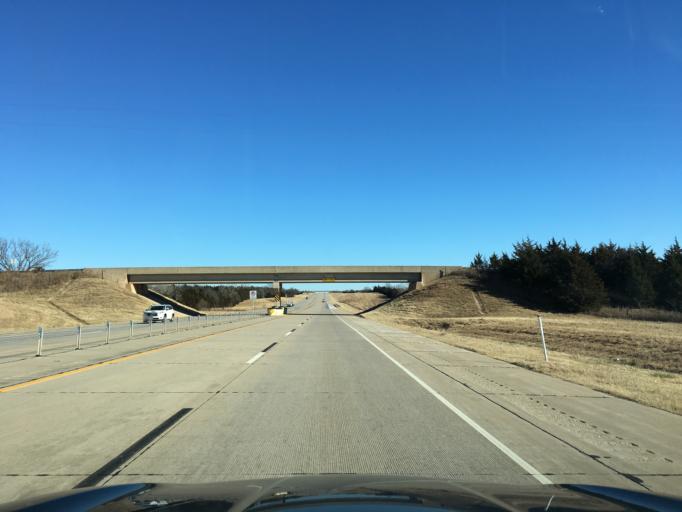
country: US
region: Oklahoma
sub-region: Payne County
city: Yale
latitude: 36.2250
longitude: -96.6793
